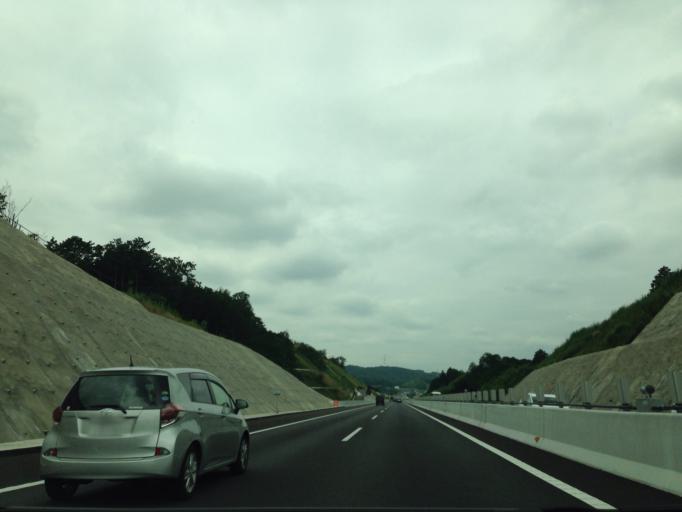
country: JP
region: Aichi
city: Gamagori
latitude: 34.9089
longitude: 137.2960
